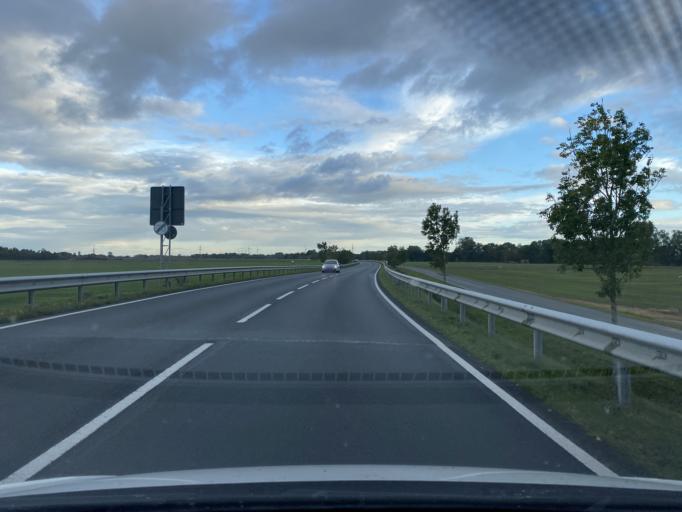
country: DE
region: Lower Saxony
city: Otterndorf
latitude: 53.7995
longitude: 8.8685
